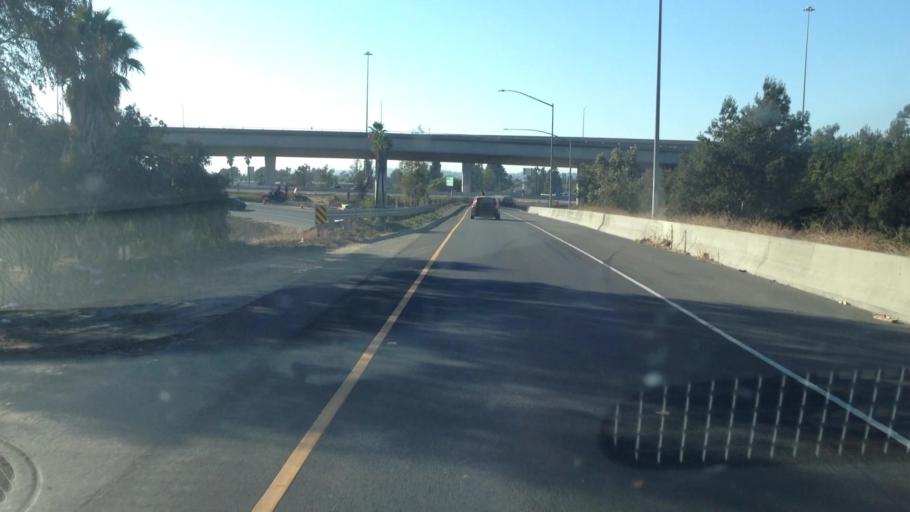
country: US
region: California
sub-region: Orange County
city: Placentia
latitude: 33.8499
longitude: -117.8739
